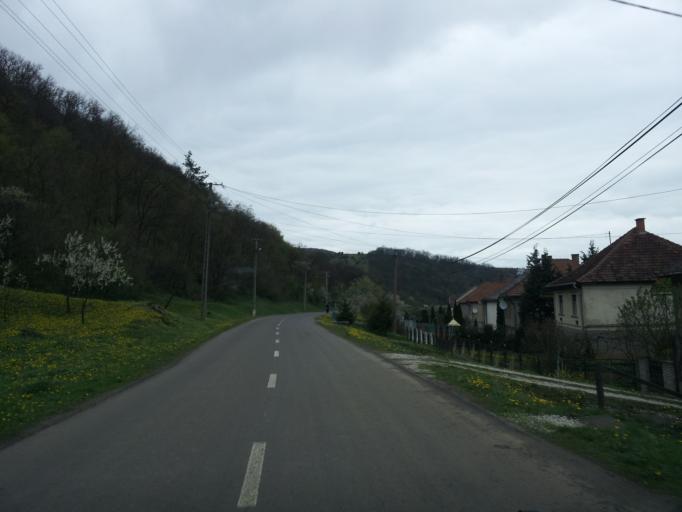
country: HU
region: Borsod-Abauj-Zemplen
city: Rudabanya
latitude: 48.4870
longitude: 20.6272
